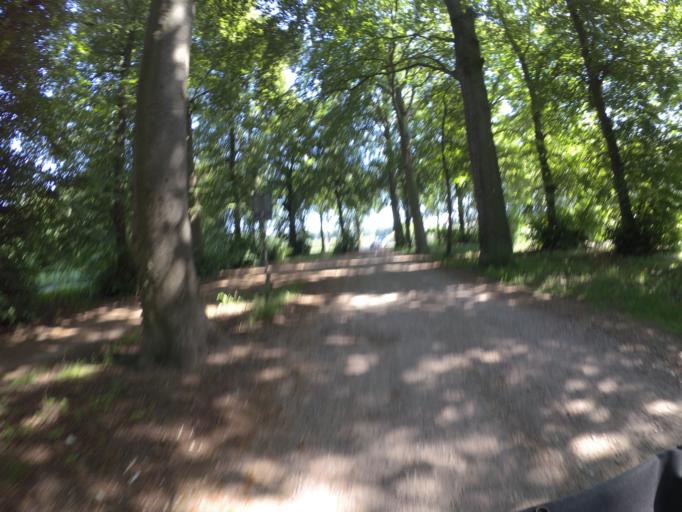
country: NL
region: North Brabant
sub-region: Gemeente Heusden
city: Heusden
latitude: 51.6900
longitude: 5.1708
